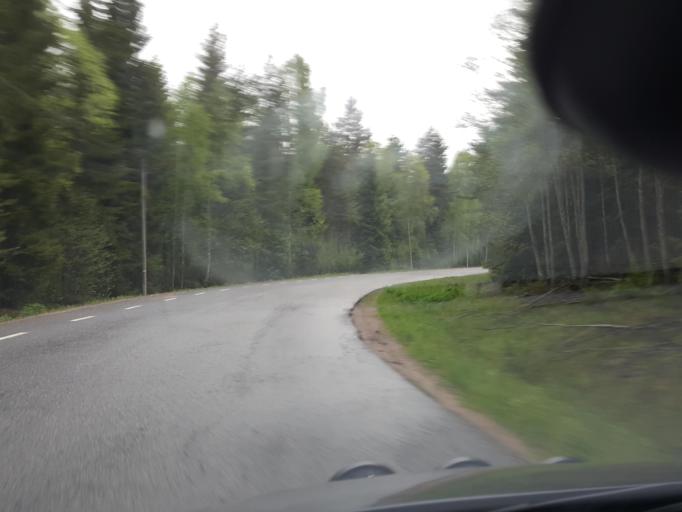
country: SE
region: Gaevleborg
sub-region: Ljusdals Kommun
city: Jaervsoe
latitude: 61.7603
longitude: 16.2048
